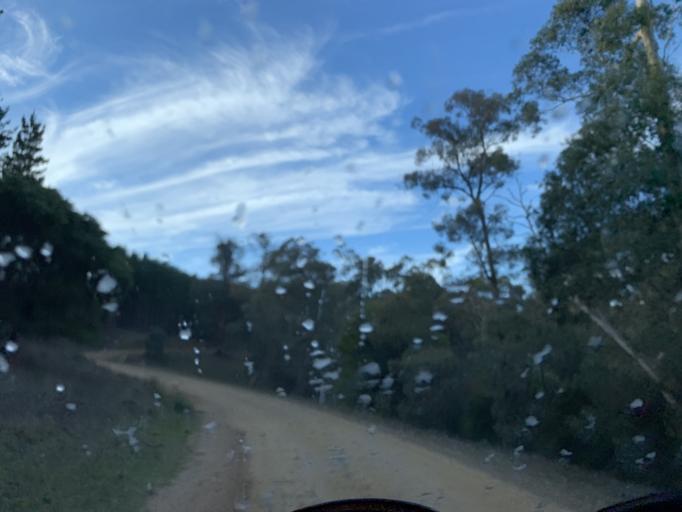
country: AU
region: Victoria
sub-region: Mansfield
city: Mansfield
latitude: -36.9254
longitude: 146.0990
